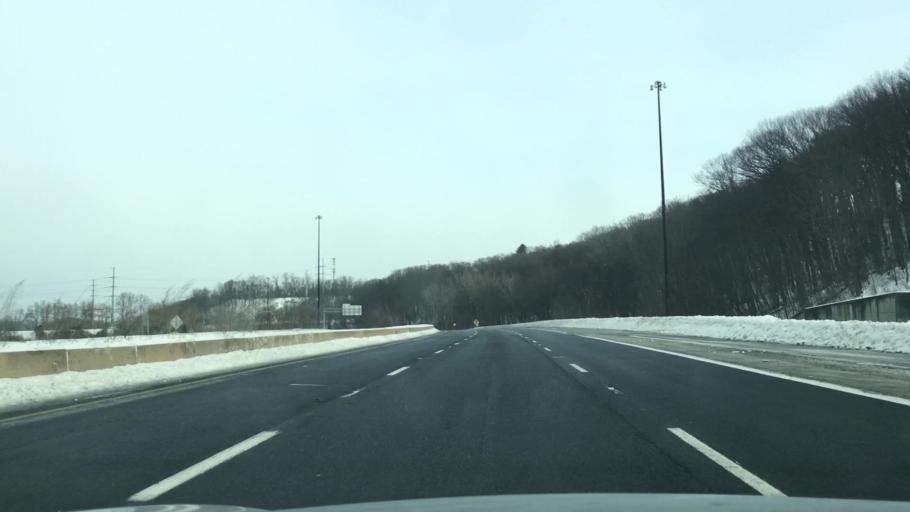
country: US
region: Massachusetts
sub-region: Hampden County
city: Chicopee
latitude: 42.1531
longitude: -72.6113
